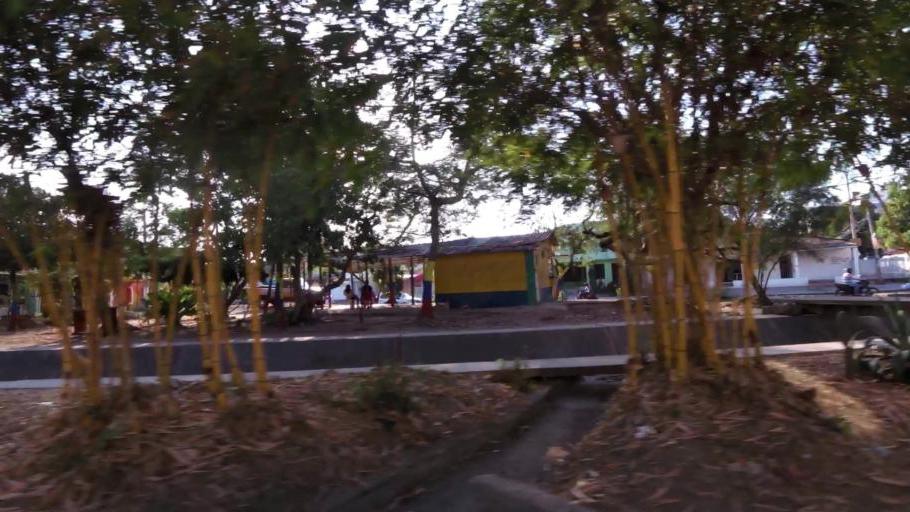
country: CO
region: Bolivar
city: Cartagena
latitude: 10.3878
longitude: -75.4814
